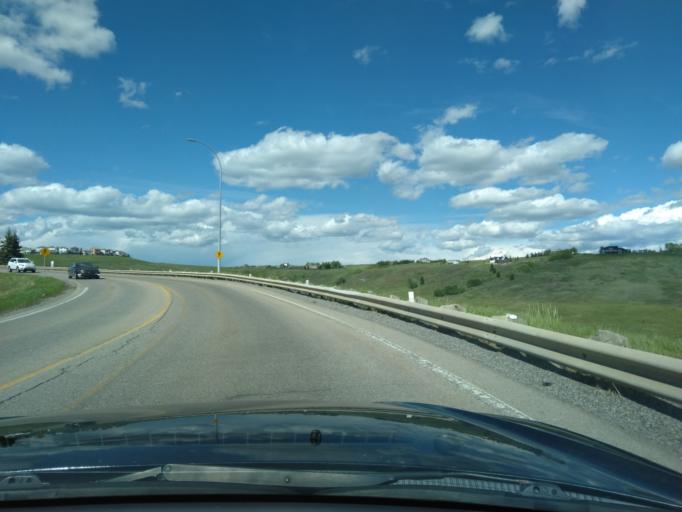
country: CA
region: Alberta
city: Cochrane
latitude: 51.1879
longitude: -114.4255
